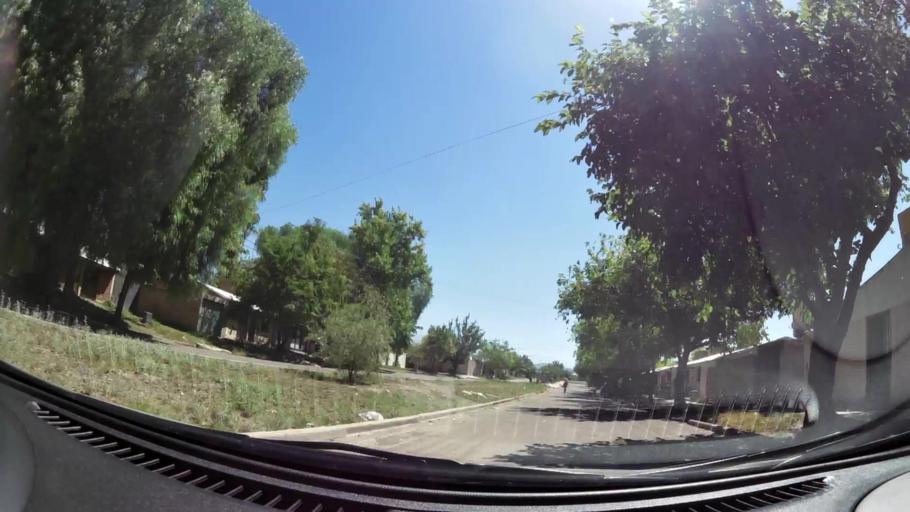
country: AR
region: Mendoza
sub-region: Departamento de Godoy Cruz
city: Godoy Cruz
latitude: -32.9328
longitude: -68.8675
